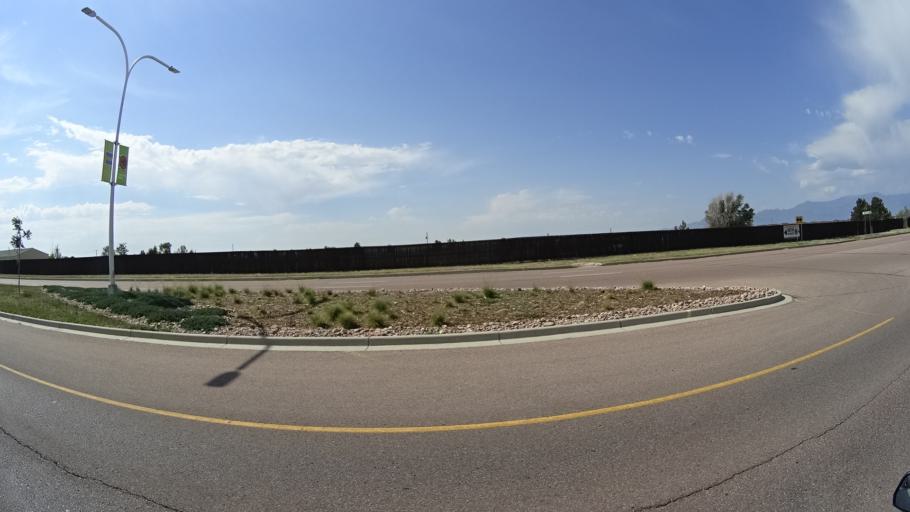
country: US
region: Colorado
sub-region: El Paso County
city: Cimarron Hills
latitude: 38.9267
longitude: -104.6774
